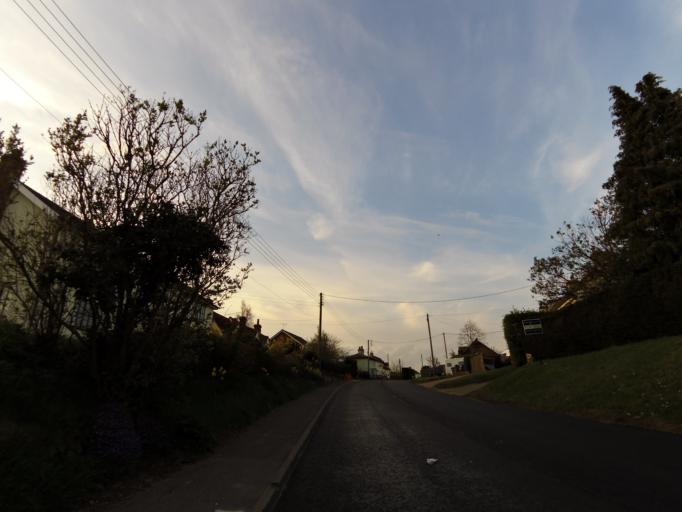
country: GB
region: England
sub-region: Suffolk
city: Ipswich
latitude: 52.1176
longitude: 1.1869
